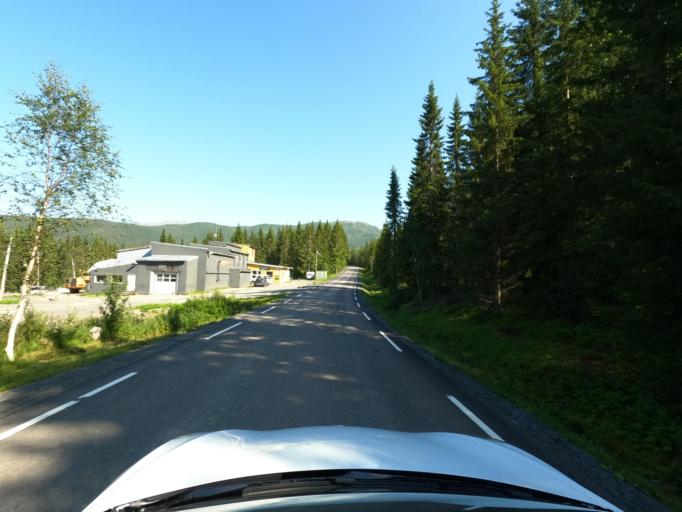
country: NO
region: Nordland
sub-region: Narvik
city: Narvik
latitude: 68.3934
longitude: 17.3214
